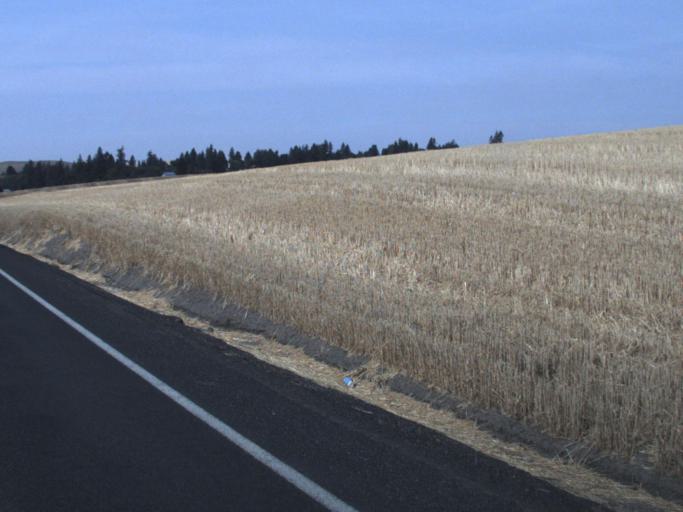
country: US
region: Idaho
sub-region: Benewah County
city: Plummer
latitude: 47.2745
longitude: -117.1412
